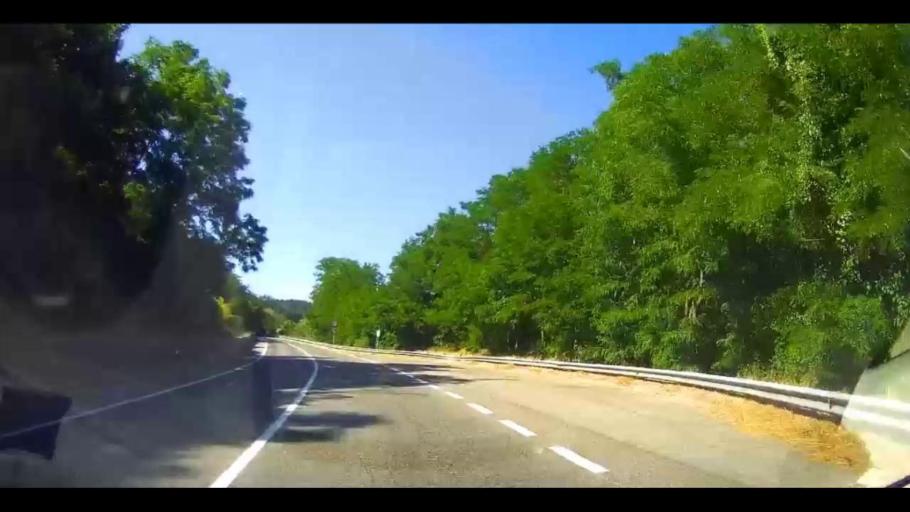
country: IT
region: Calabria
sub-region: Provincia di Cosenza
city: Spezzano Piccolo
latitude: 39.2956
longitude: 16.3548
